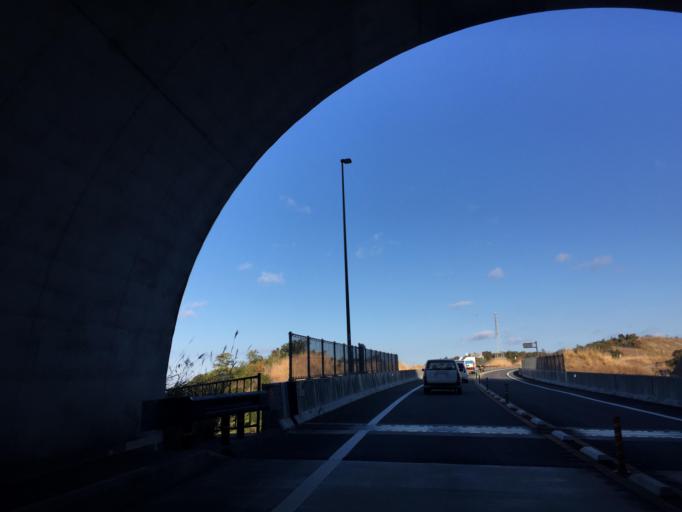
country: JP
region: Wakayama
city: Wakayama-shi
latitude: 34.3105
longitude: 135.1612
